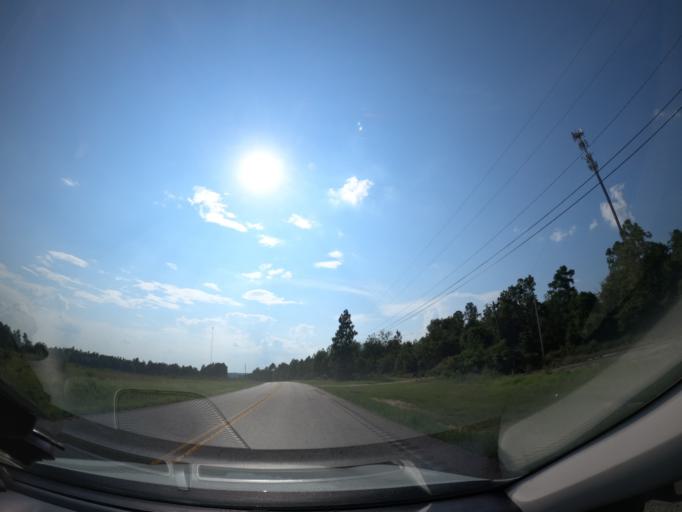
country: US
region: South Carolina
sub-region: Aiken County
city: Jackson
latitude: 33.4115
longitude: -81.8031
